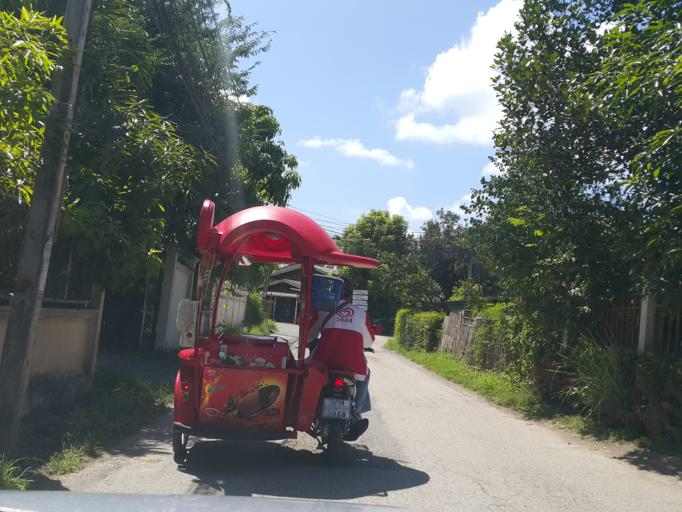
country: TH
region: Chiang Mai
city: San Kamphaeng
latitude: 18.7224
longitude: 99.0975
